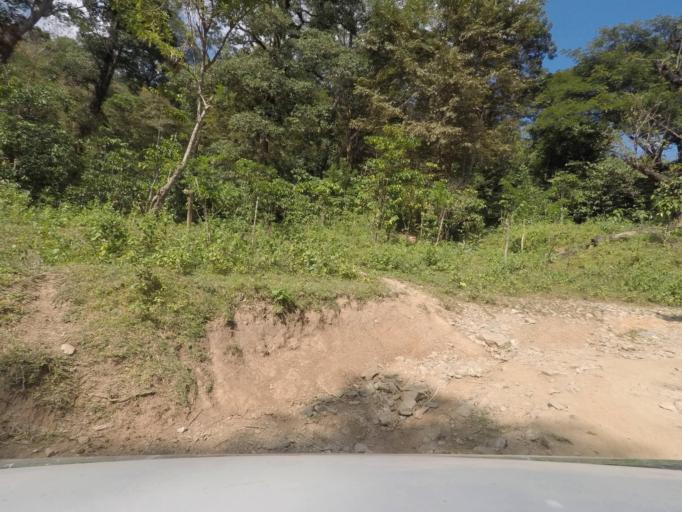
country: TL
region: Ermera
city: Gleno
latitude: -8.7182
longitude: 125.3068
